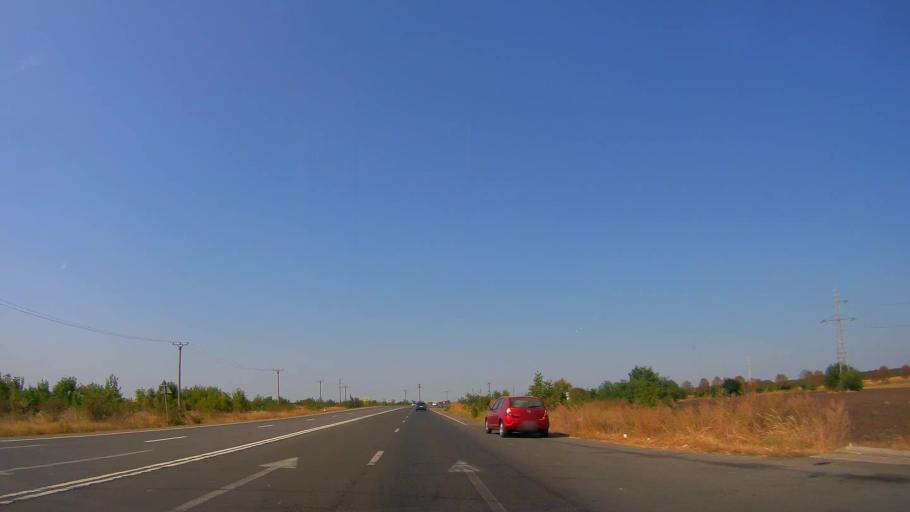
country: RO
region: Giurgiu
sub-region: Comuna Daia
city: Plopsoru
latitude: 44.0201
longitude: 25.9739
